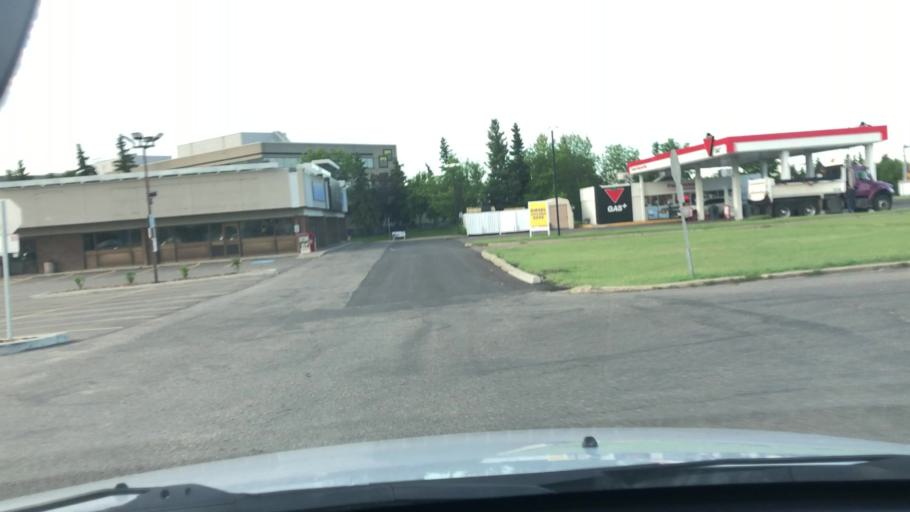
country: CA
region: Alberta
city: Edmonton
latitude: 53.5385
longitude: -113.4174
